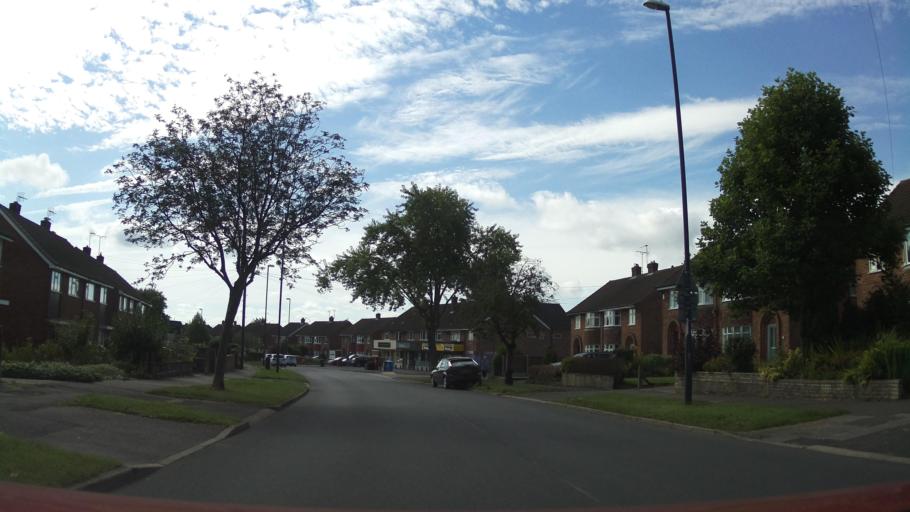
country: GB
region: England
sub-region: Derbyshire
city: Duffield
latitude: 52.9528
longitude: -1.5018
